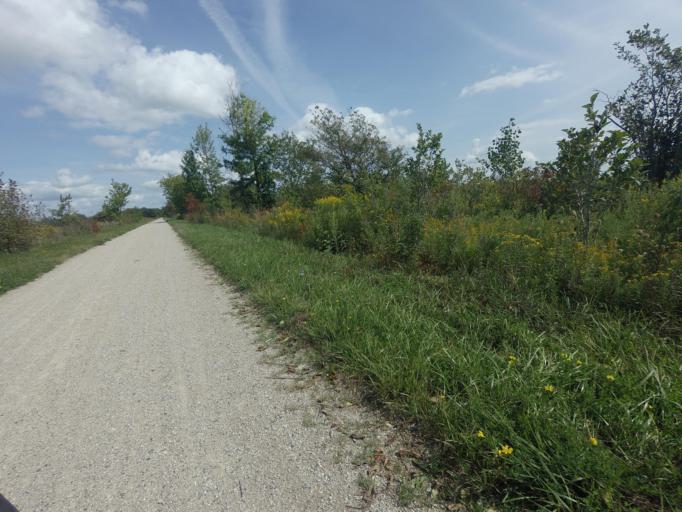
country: CA
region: Ontario
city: Waterloo
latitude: 43.5851
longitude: -80.7176
